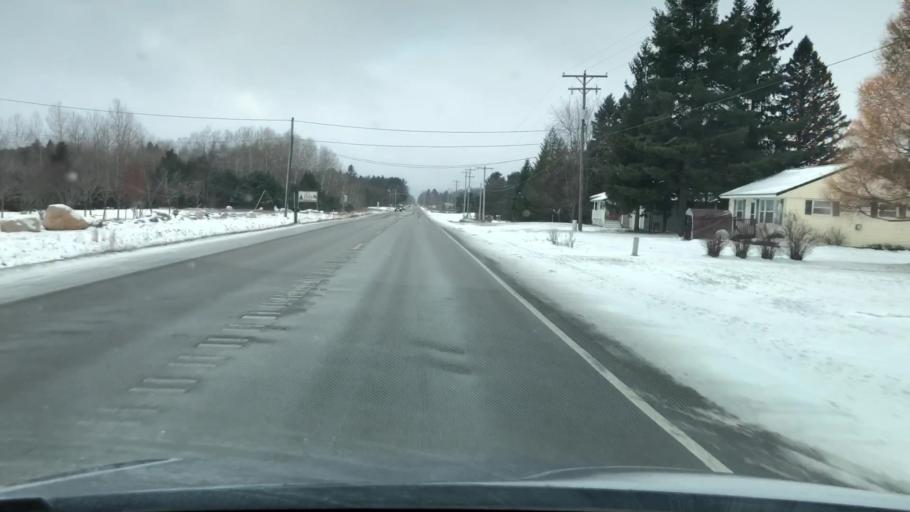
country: US
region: Michigan
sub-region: Wexford County
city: Cadillac
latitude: 44.2812
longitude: -85.4529
